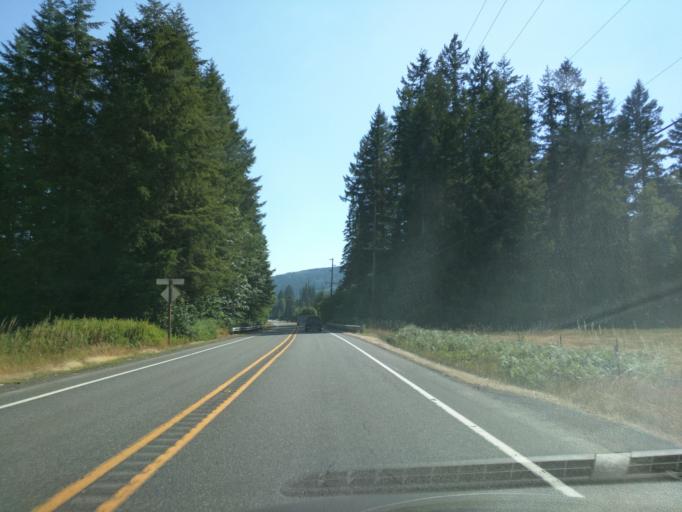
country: US
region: Washington
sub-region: Whatcom County
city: Peaceful Valley
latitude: 48.8976
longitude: -122.1465
